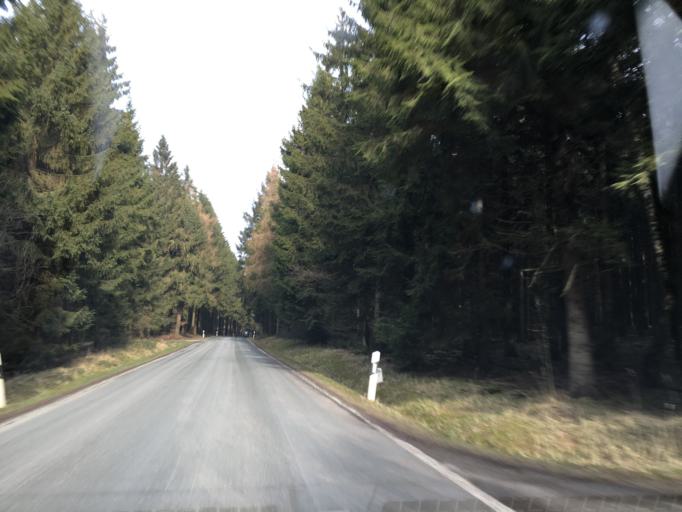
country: DE
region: North Rhine-Westphalia
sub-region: Regierungsbezirk Detmold
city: Willebadessen
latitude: 51.6034
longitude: 8.9917
